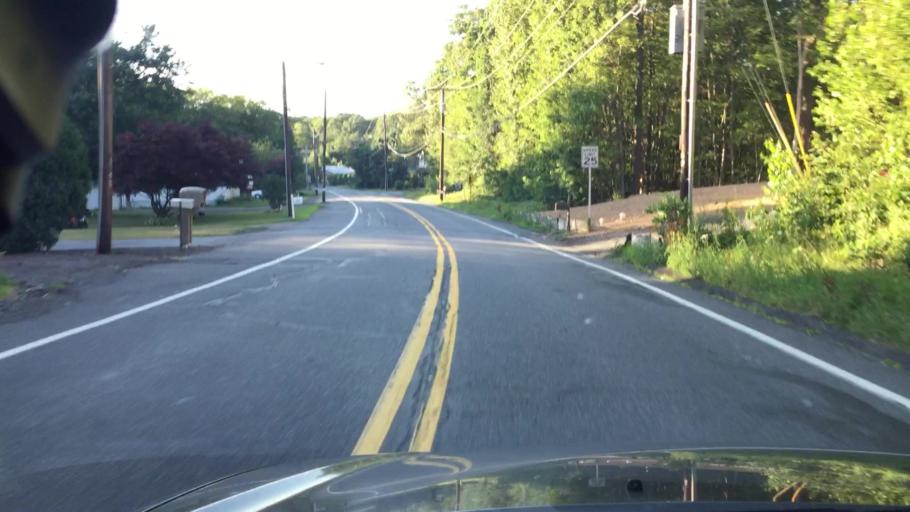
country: US
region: Pennsylvania
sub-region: Luzerne County
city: Harleigh
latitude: 40.9852
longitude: -75.9755
